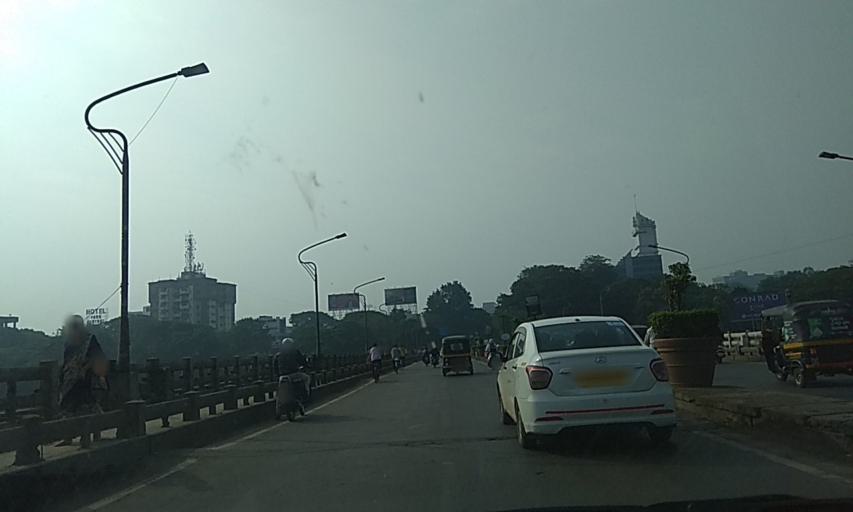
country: IN
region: Maharashtra
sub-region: Pune Division
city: Shivaji Nagar
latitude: 18.5436
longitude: 73.8850
